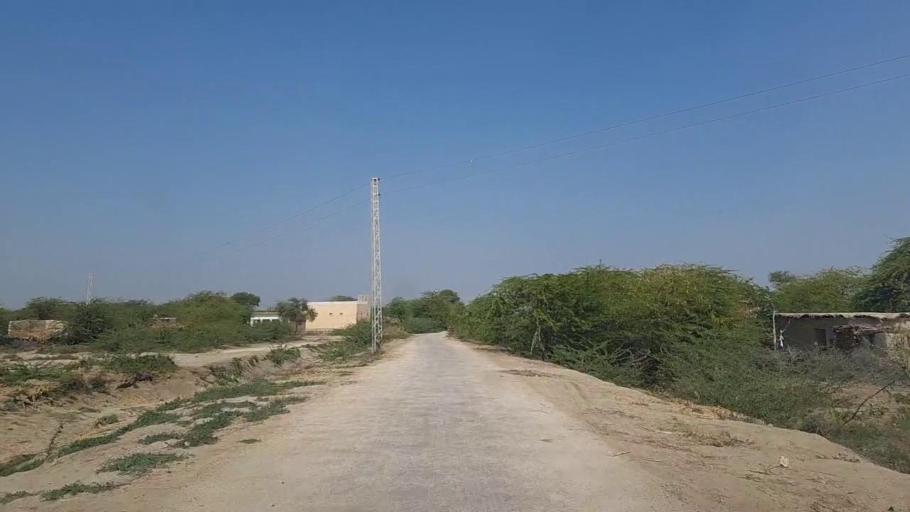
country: PK
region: Sindh
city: Naukot
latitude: 24.8723
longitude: 69.3842
